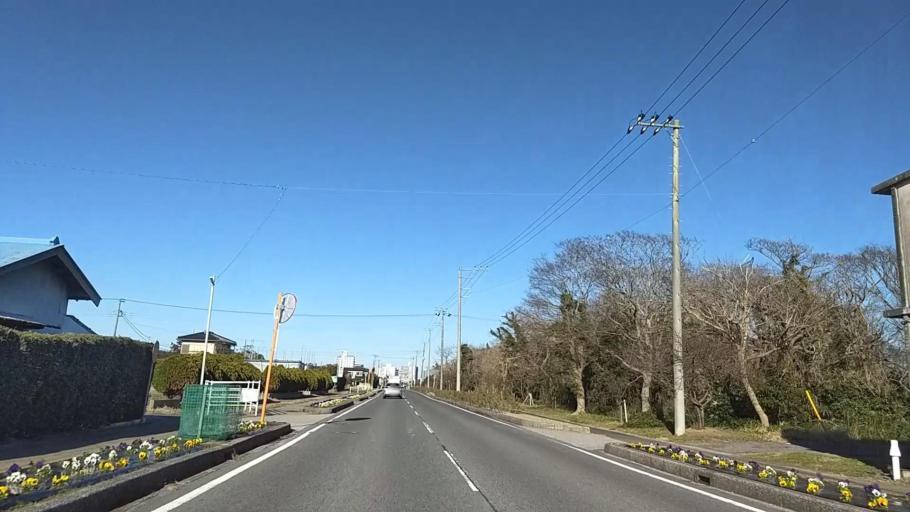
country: JP
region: Chiba
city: Mobara
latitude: 35.4403
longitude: 140.3993
